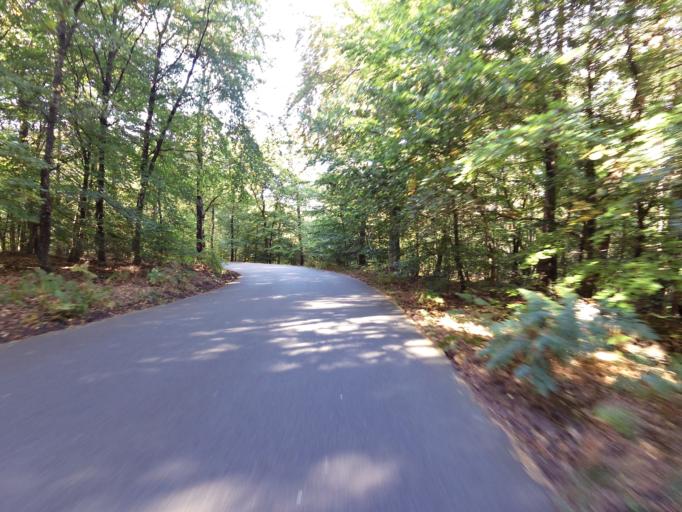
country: NL
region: Gelderland
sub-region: Gemeente Rheden
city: Rheden
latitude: 52.0247
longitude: 5.9981
